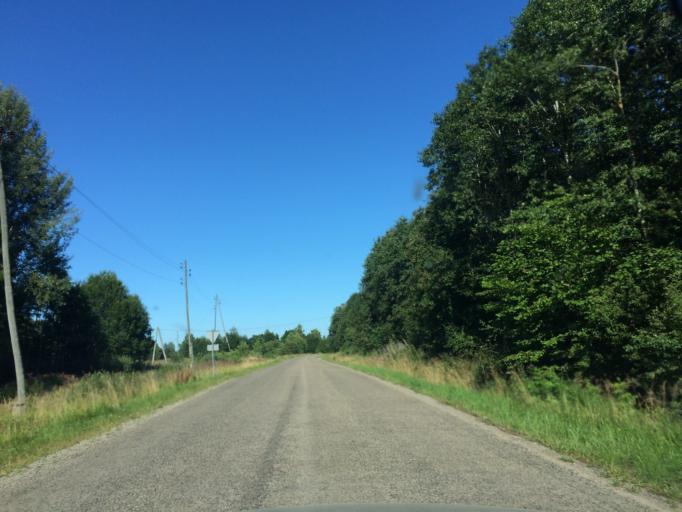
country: LV
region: Rezekne
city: Rezekne
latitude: 56.4919
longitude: 27.2719
